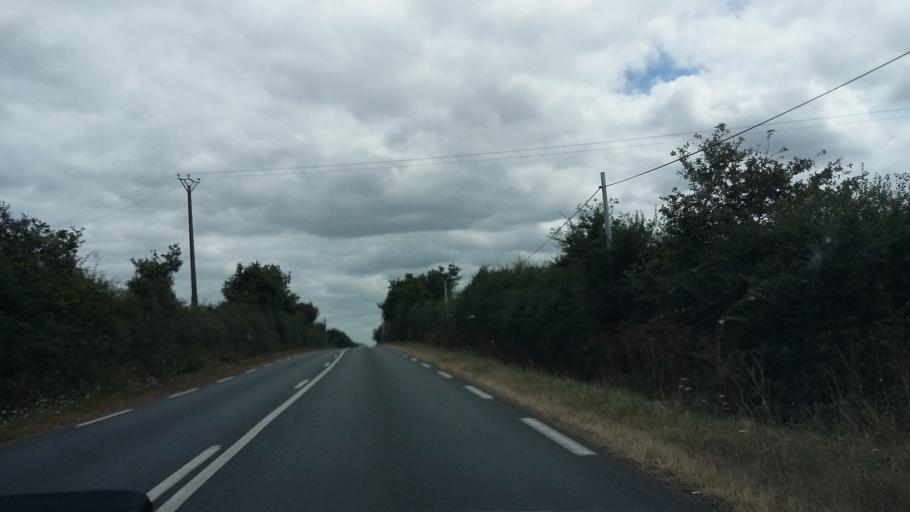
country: FR
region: Pays de la Loire
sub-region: Departement de la Vendee
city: Mache
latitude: 46.7802
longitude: -1.6861
